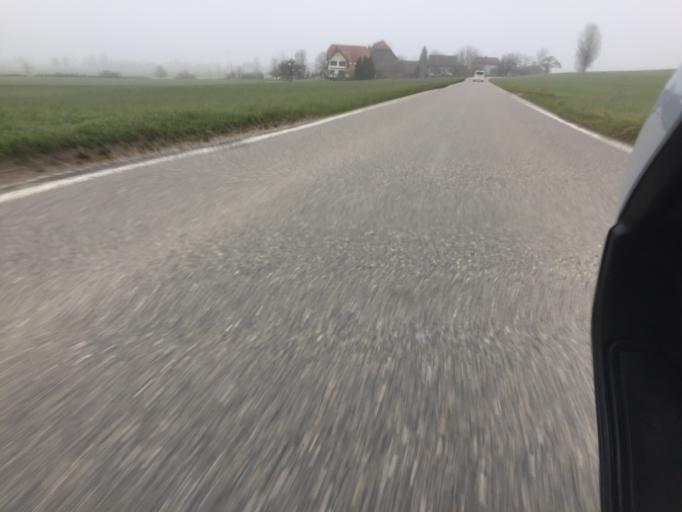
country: CH
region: Bern
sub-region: Seeland District
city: Grossaffoltern
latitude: 47.0830
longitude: 7.3862
